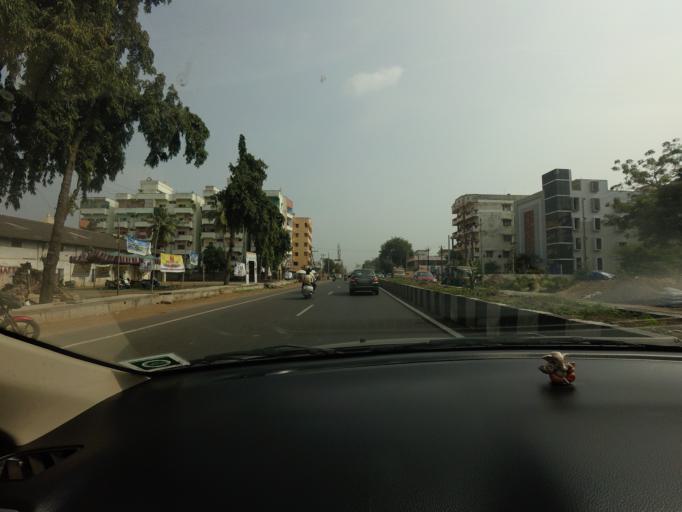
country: IN
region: Andhra Pradesh
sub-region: Krishna
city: Yanamalakuduru
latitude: 16.4850
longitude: 80.6834
